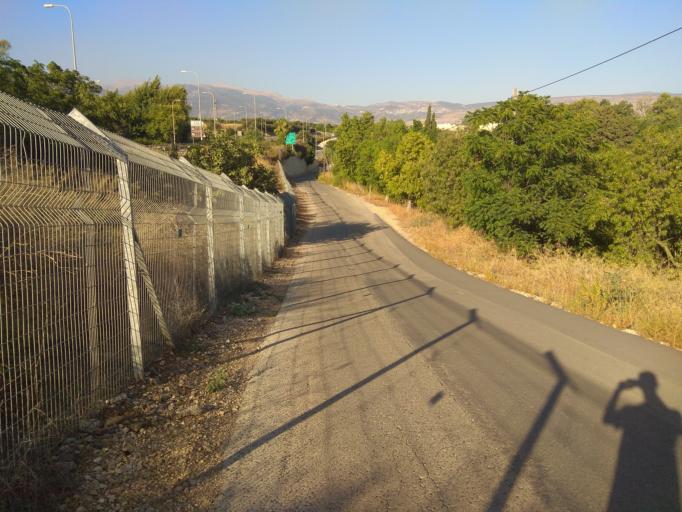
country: IL
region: Northern District
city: Qiryat Shemona
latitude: 33.2235
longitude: 35.6196
